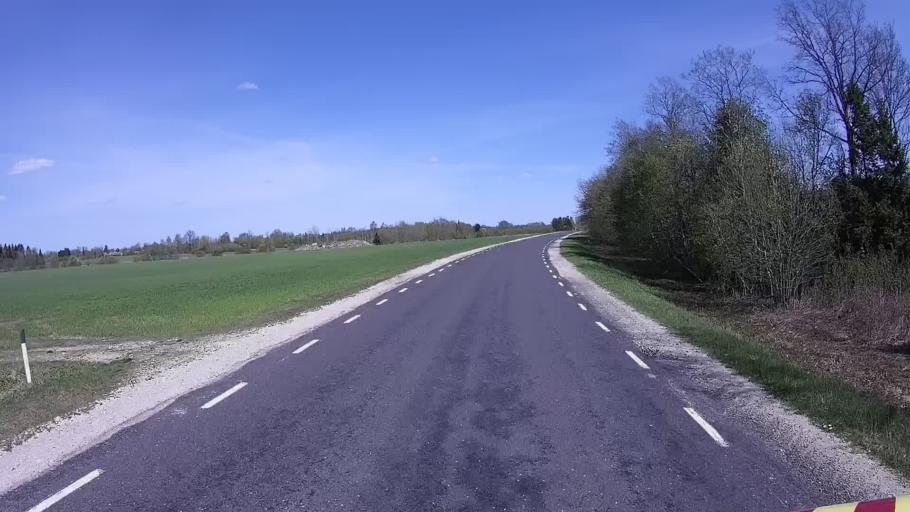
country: EE
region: Laeaene
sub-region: Ridala Parish
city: Uuemoisa
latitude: 59.0118
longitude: 23.7845
